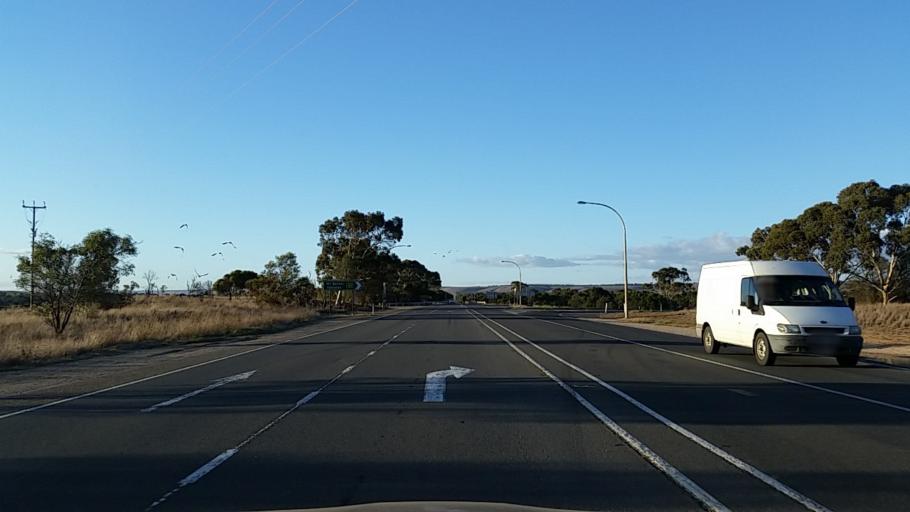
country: AU
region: South Australia
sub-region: Mount Barker
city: Callington
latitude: -35.1291
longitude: 139.0355
